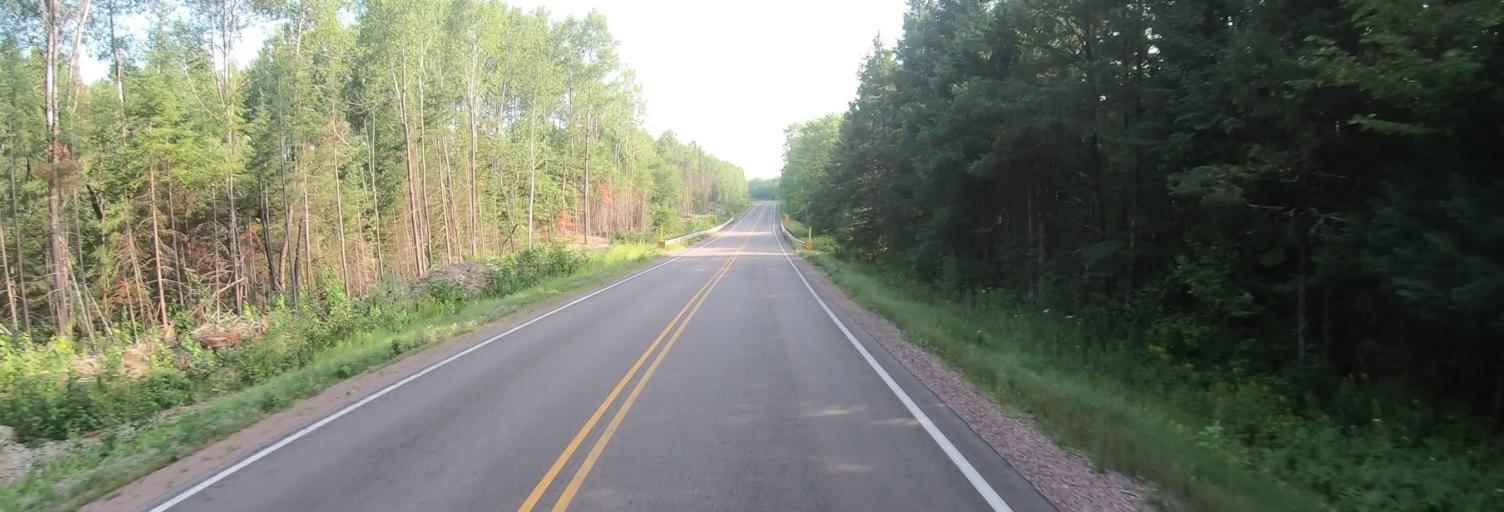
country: US
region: Wisconsin
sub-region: Ashland County
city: Ashland
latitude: 46.2700
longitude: -90.8397
